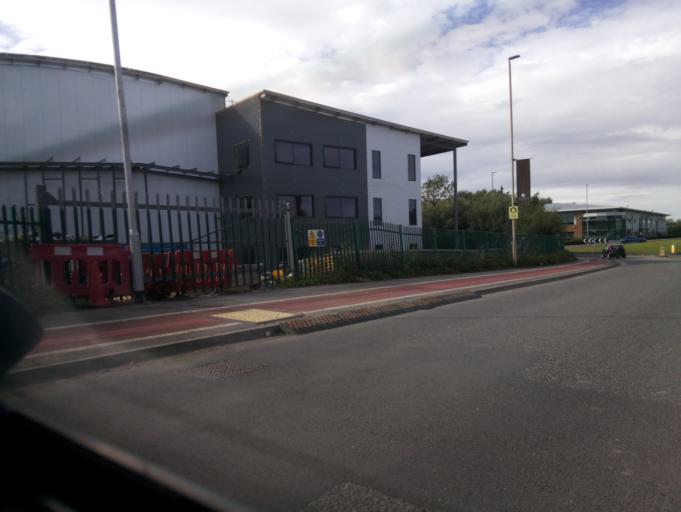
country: GB
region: England
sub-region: Gloucestershire
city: Gloucester
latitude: 51.8111
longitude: -2.2684
